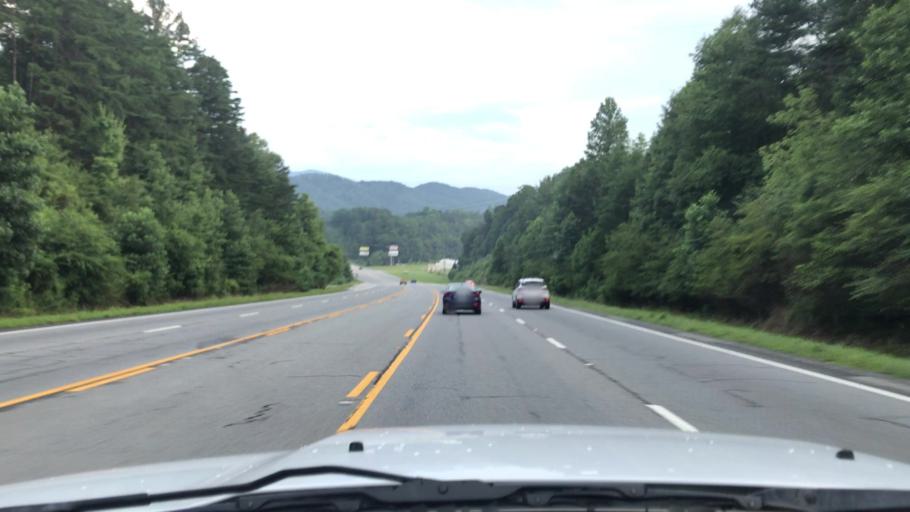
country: US
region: Georgia
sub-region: Fannin County
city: Blue Ridge
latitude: 34.8579
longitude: -84.3364
